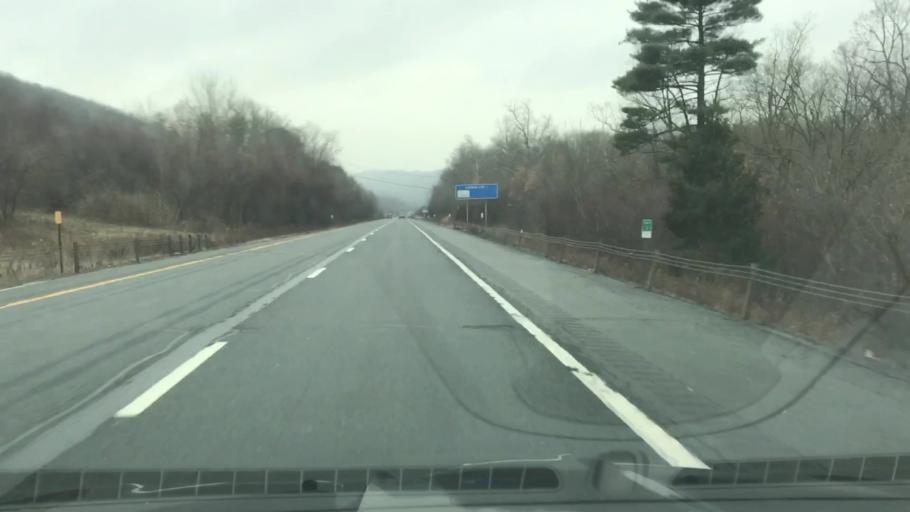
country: US
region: New York
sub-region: Orange County
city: Port Jervis
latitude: 41.3584
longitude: -74.6652
